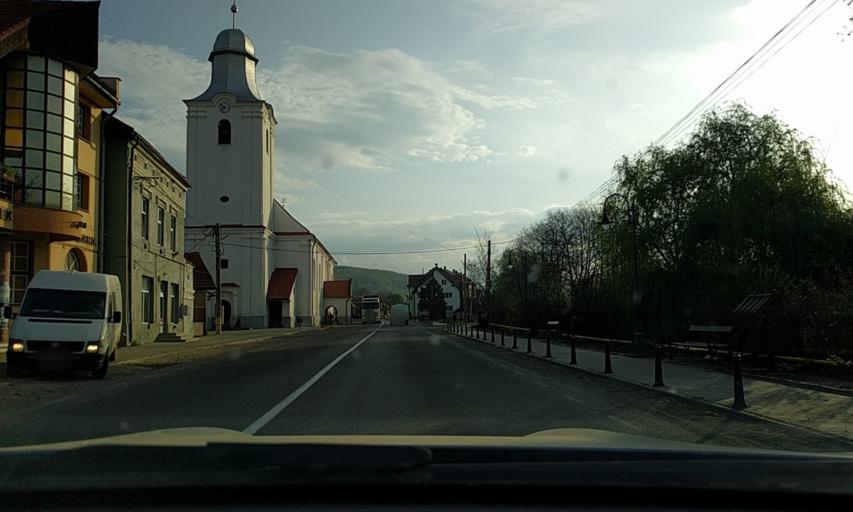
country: RO
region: Covasna
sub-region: Comuna Bretcu
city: Bretcu
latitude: 46.0434
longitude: 26.3011
